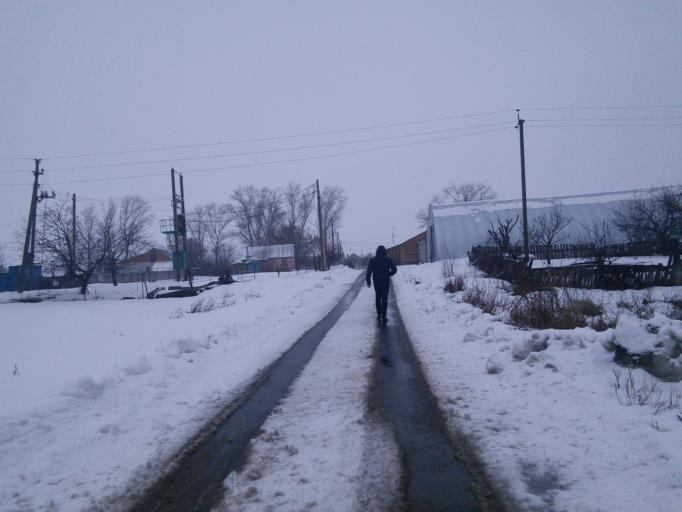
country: RU
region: Kursk
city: Chernitsyno
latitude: 51.5759
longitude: 36.0815
